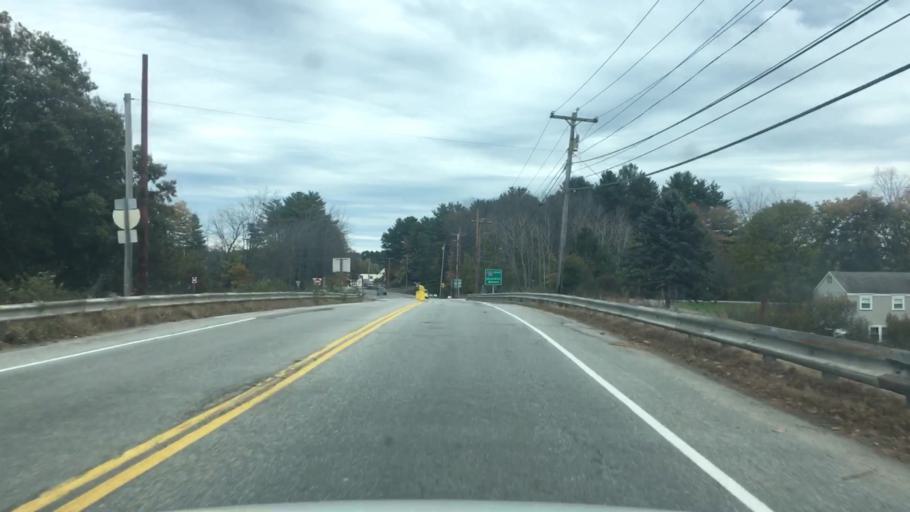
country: US
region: Maine
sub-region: Cumberland County
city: Falmouth
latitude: 43.7274
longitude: -70.2363
